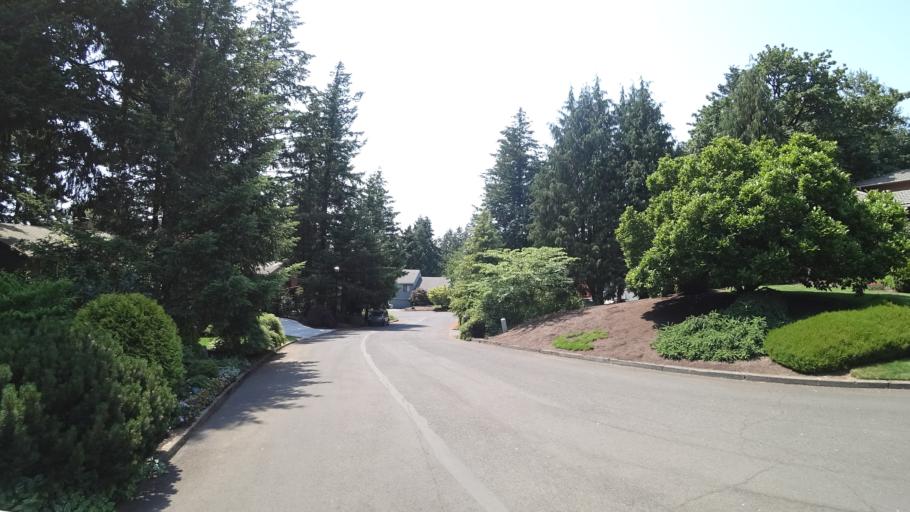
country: US
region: Oregon
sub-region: Clackamas County
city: Happy Valley
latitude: 45.4496
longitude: -122.5594
